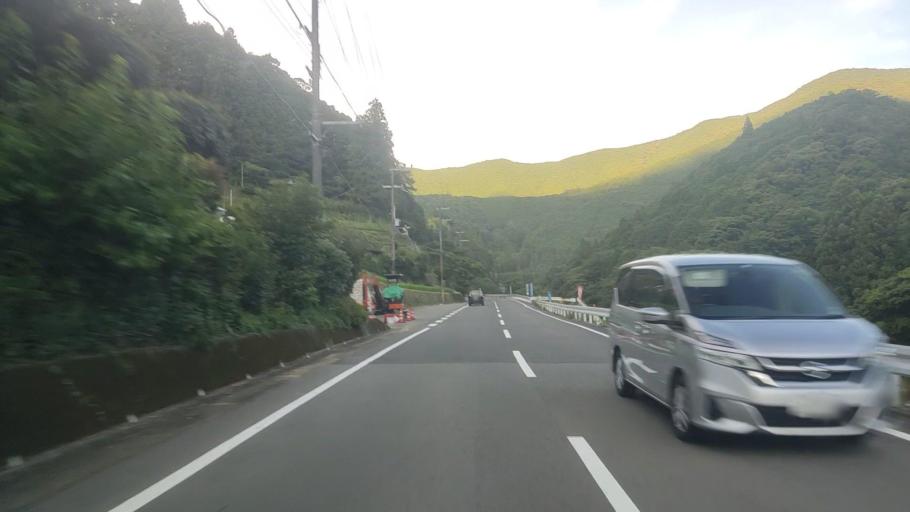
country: JP
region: Wakayama
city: Tanabe
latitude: 33.8110
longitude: 135.5439
